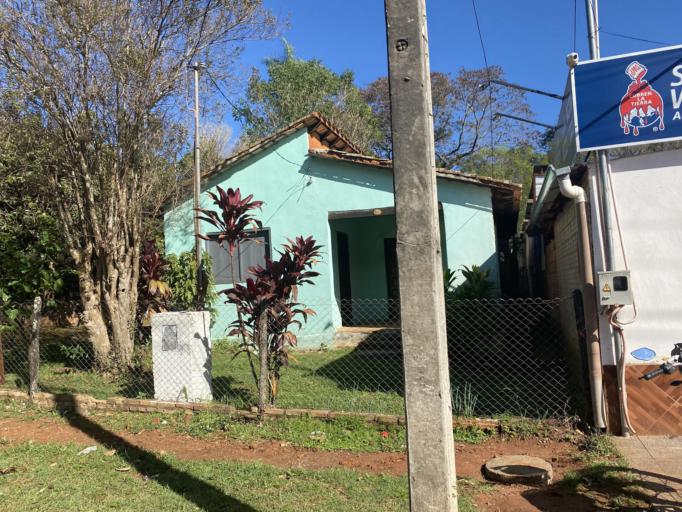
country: PY
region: Misiones
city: San Juan Bautista
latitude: -26.6667
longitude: -57.1379
